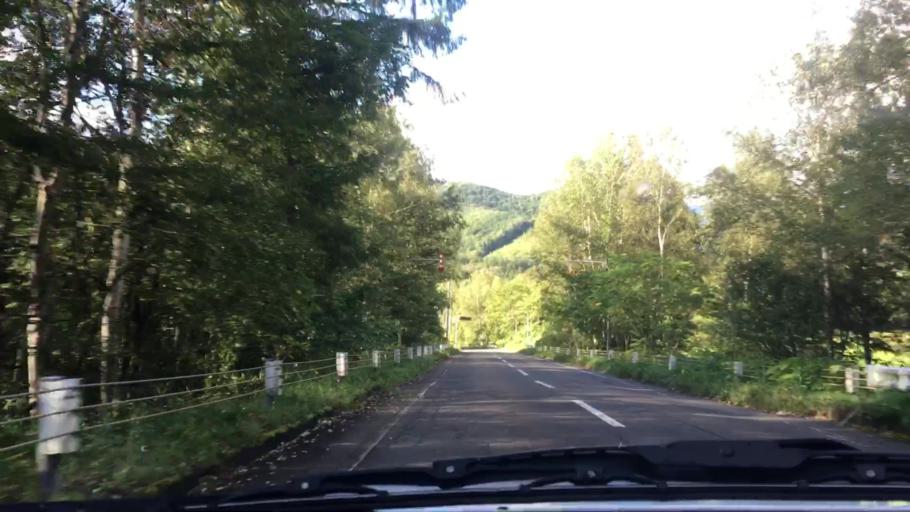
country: JP
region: Hokkaido
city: Otofuke
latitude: 43.1802
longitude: 142.9292
